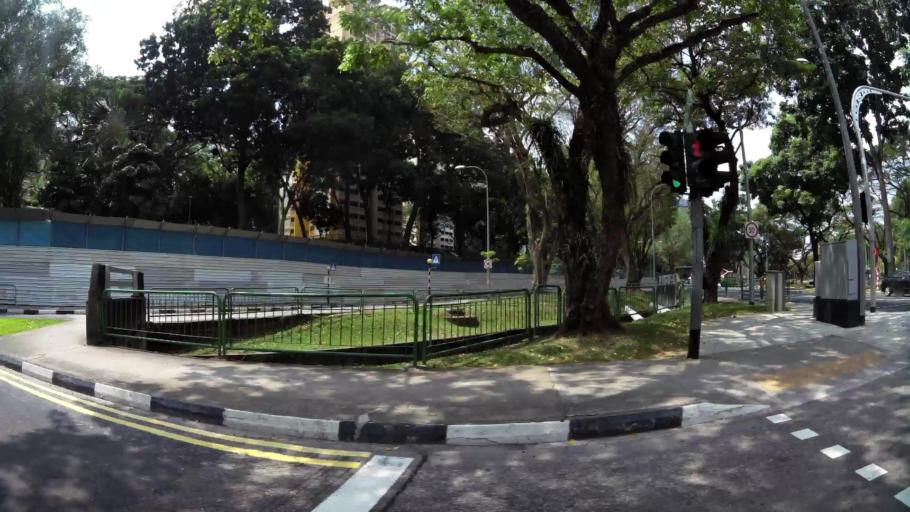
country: SG
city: Singapore
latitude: 1.2863
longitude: 103.8251
